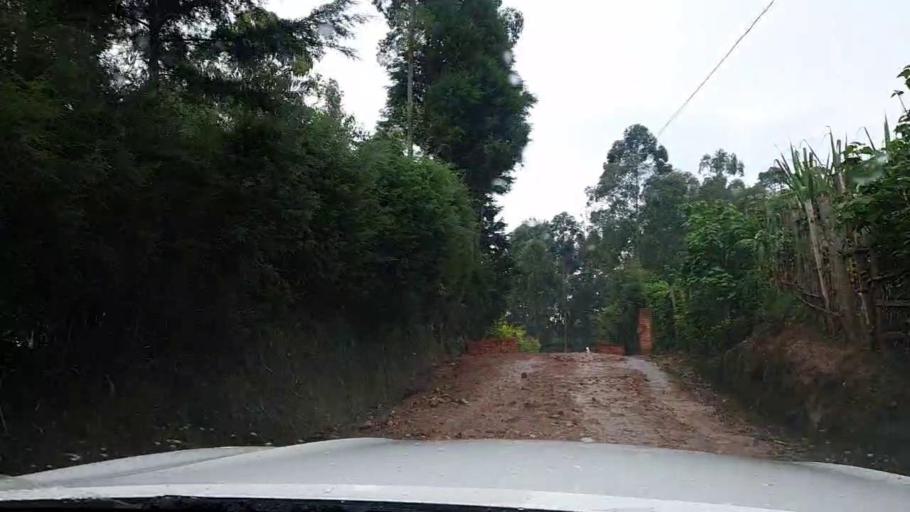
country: RW
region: Western Province
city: Cyangugu
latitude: -2.5459
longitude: 28.9787
